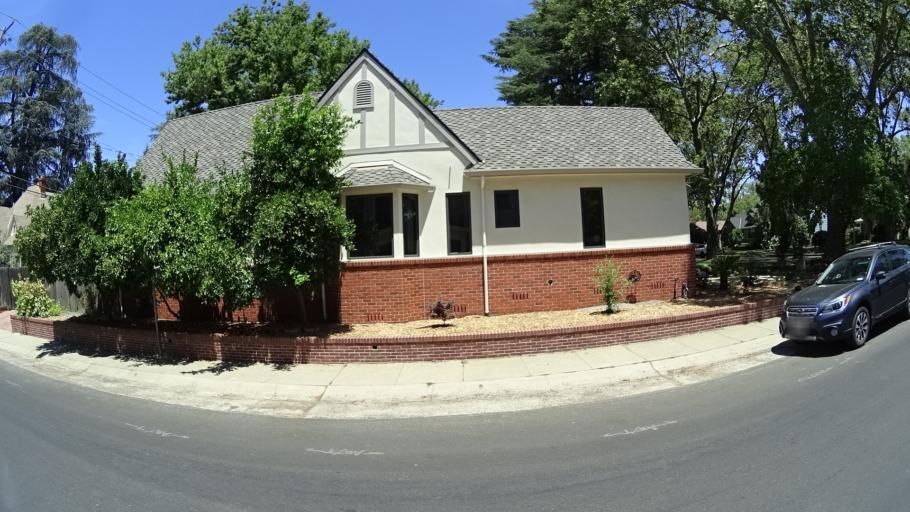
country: US
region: California
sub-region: Sacramento County
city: Sacramento
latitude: 38.5668
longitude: -121.4543
